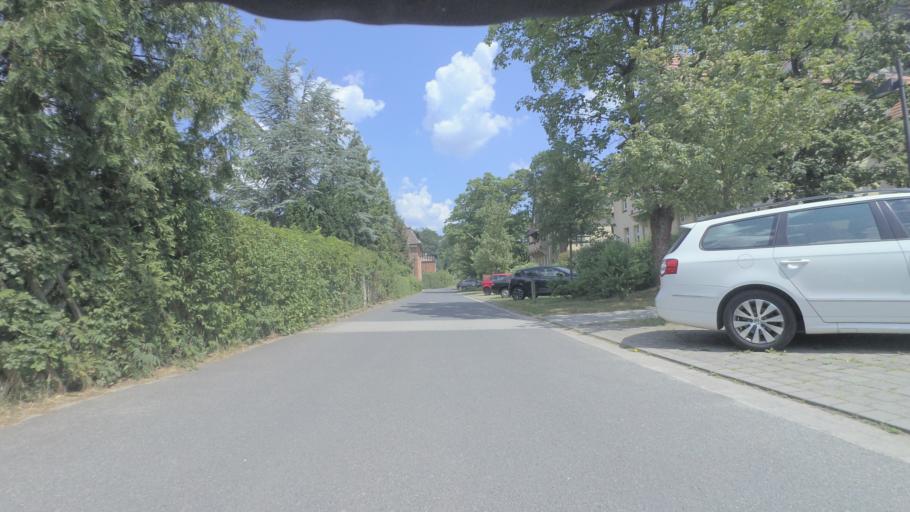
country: DE
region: Brandenburg
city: Fichtenwalde
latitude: 52.2601
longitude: 12.9231
